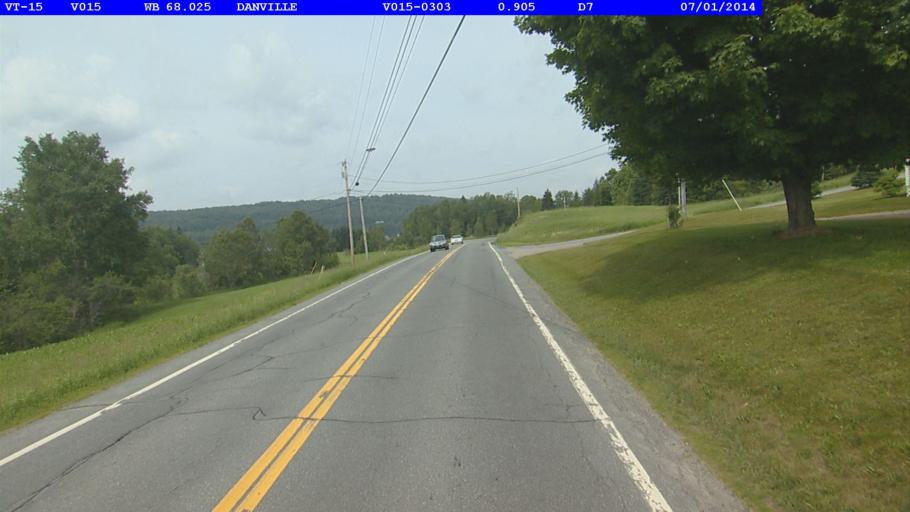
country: US
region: Vermont
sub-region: Caledonia County
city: Hardwick
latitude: 44.4115
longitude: -72.2128
